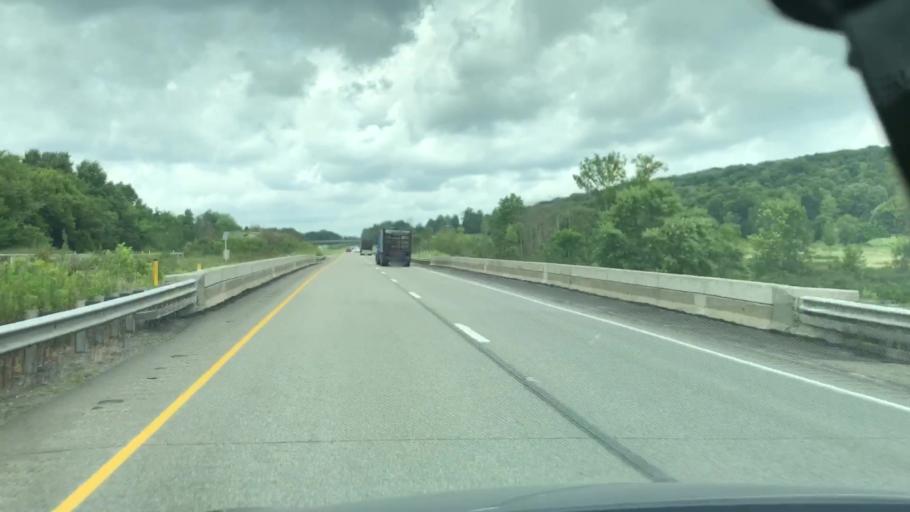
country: US
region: Pennsylvania
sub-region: Crawford County
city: Meadville
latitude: 41.6620
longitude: -80.2069
